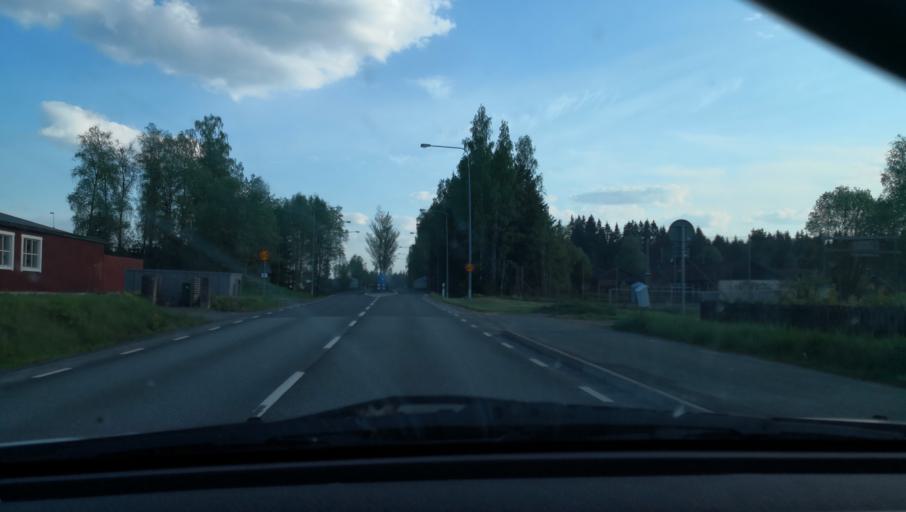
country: SE
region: Joenkoeping
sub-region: Nassjo Kommun
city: Bodafors
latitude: 57.5624
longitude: 14.6961
